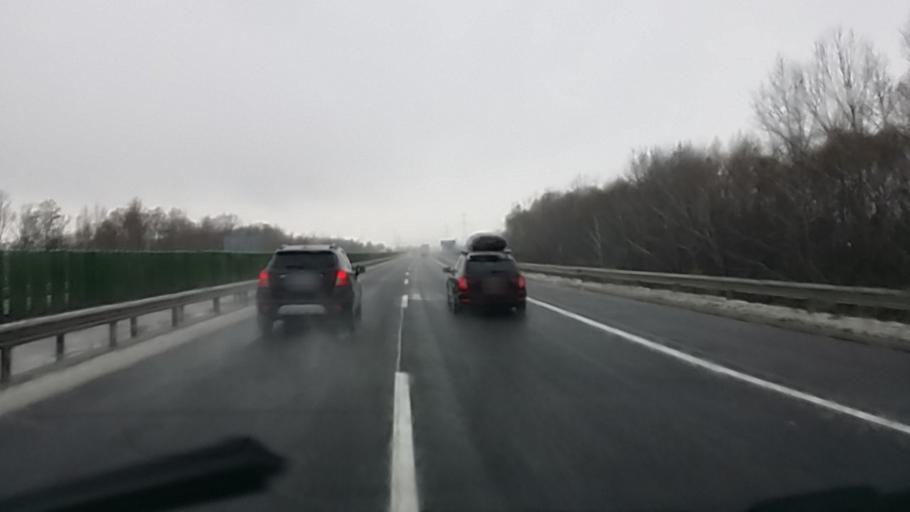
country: HU
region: Gyor-Moson-Sopron
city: Abda
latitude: 47.6811
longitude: 17.5426
